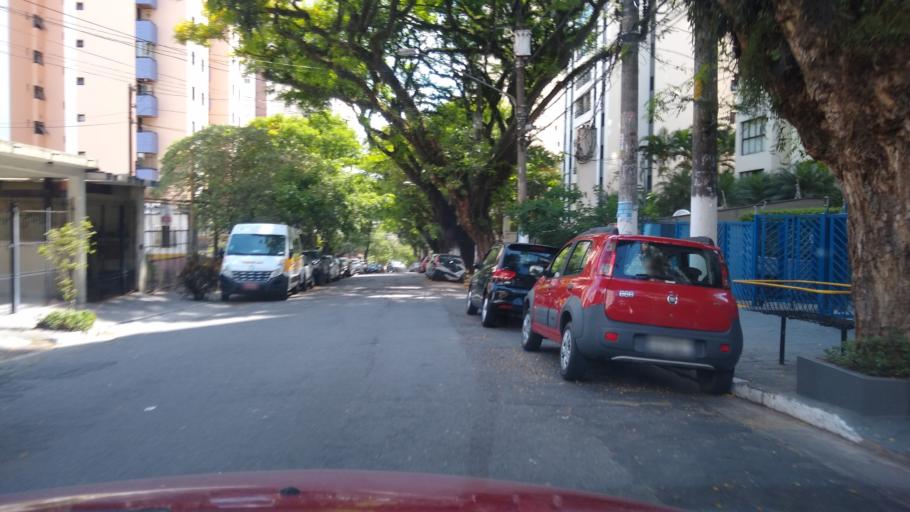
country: BR
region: Sao Paulo
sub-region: Diadema
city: Diadema
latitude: -23.6471
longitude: -46.6663
